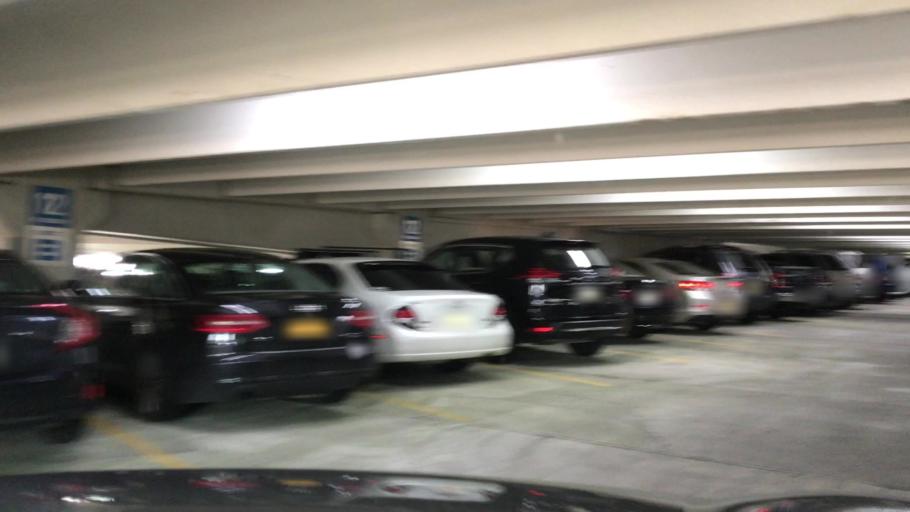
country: US
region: New Jersey
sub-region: Atlantic County
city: Atlantic City
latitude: 39.3588
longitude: -74.4404
